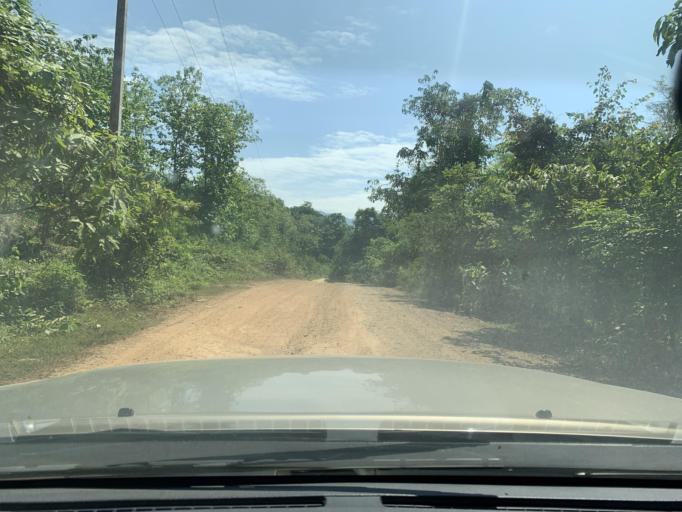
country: LA
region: Louangphabang
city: Louangphabang
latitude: 19.8934
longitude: 102.2047
